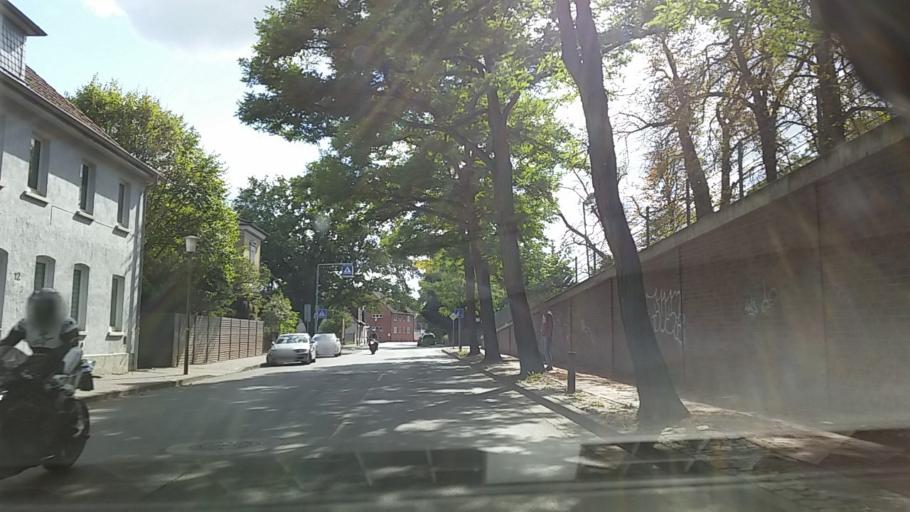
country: DE
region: Lower Saxony
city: Uelzen
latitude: 52.9693
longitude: 10.5557
